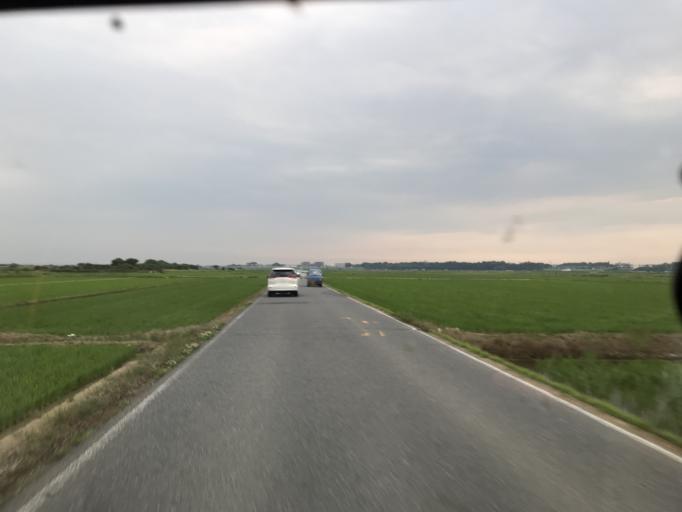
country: JP
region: Chiba
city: Abiko
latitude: 35.8949
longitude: 140.0225
